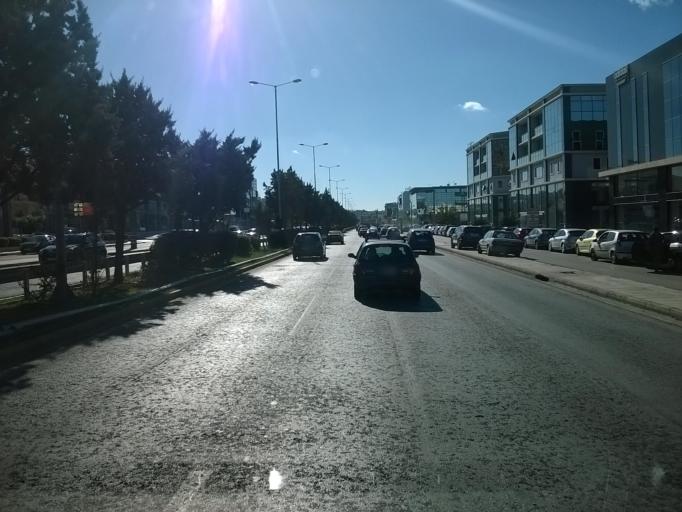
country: GR
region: Attica
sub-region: Nomarchia Athinas
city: Glyfada
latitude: 37.8664
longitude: 23.7607
